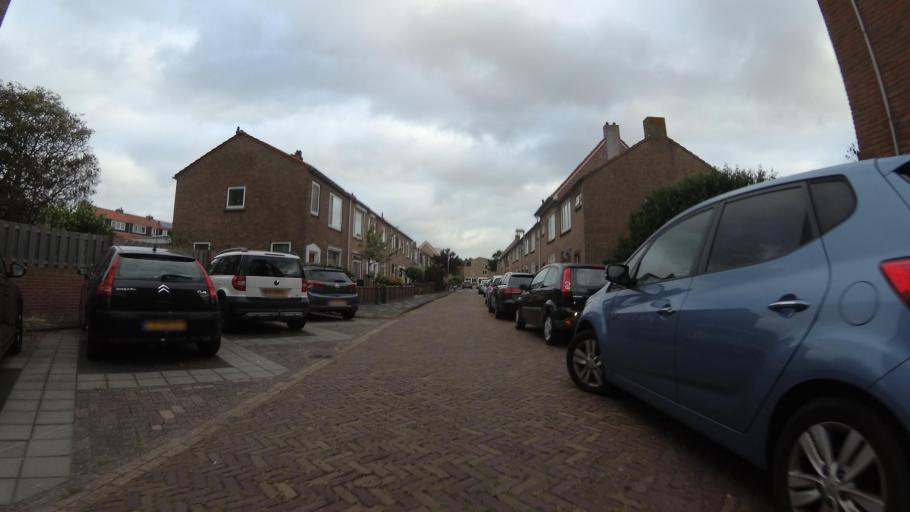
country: NL
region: North Holland
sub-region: Gemeente Den Helder
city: Den Helder
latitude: 52.9607
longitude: 4.7471
